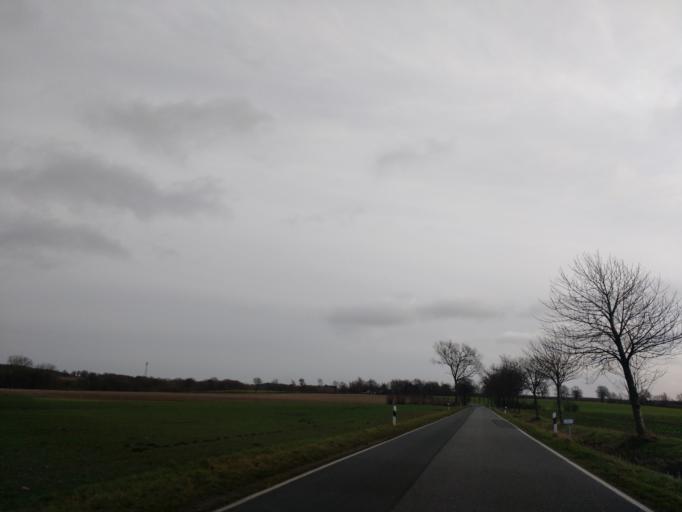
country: DE
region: Schleswig-Holstein
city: Susel
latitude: 54.0139
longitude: 10.6628
